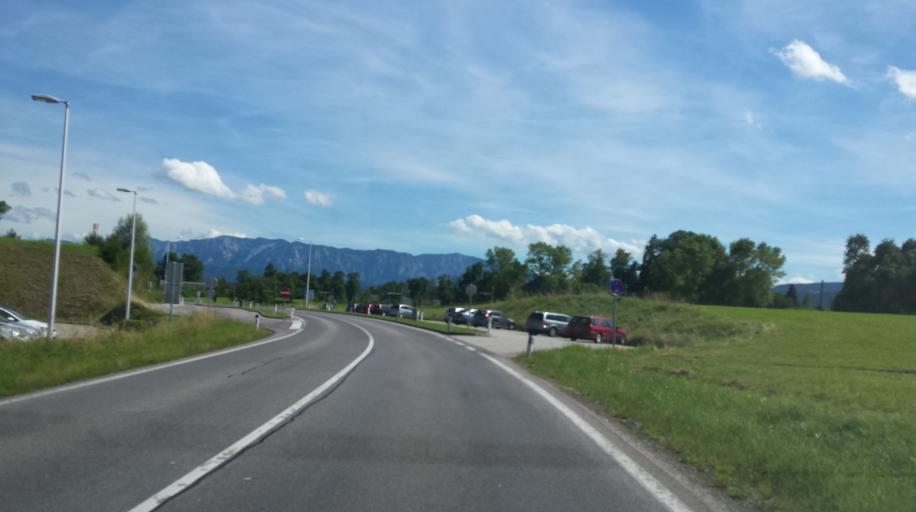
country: AT
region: Upper Austria
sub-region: Politischer Bezirk Vocklabruck
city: Sankt Georgen im Attergau
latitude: 47.9291
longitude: 13.5024
